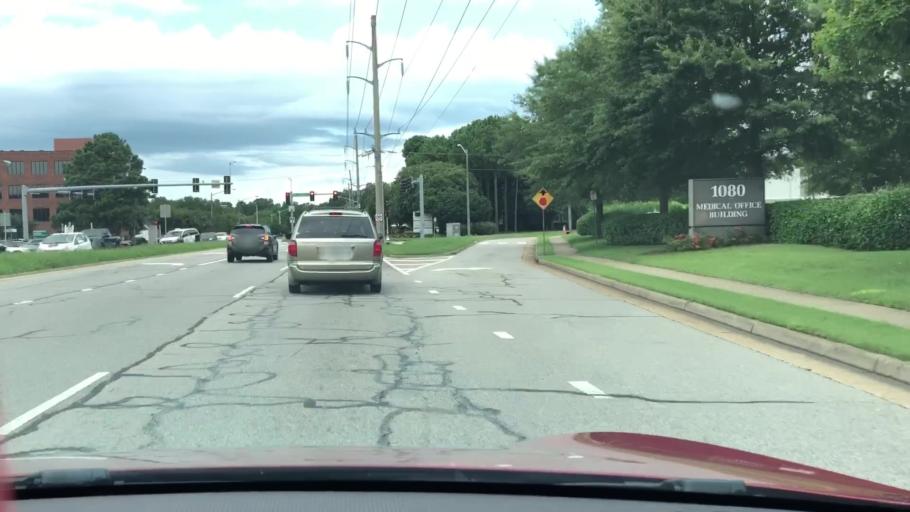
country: US
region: Virginia
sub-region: City of Virginia Beach
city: Virginia Beach
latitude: 36.8649
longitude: -76.0287
